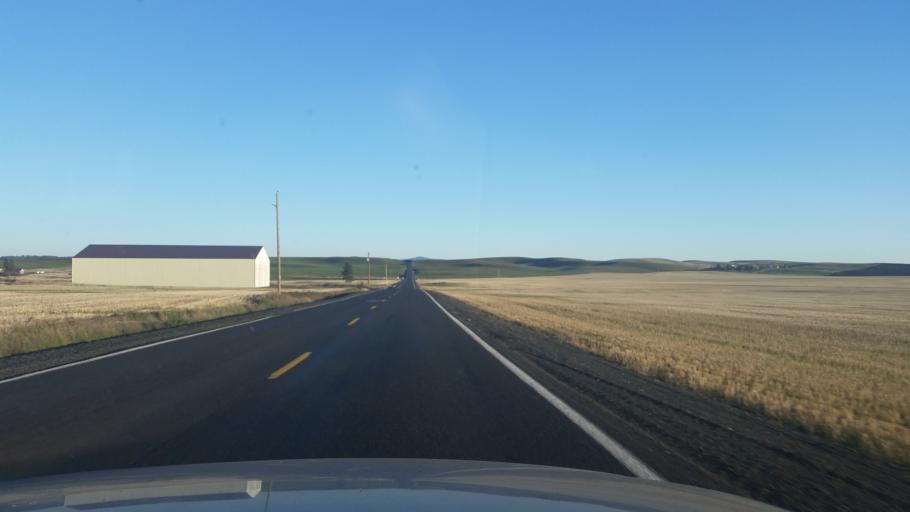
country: US
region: Washington
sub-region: Spokane County
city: Opportunity
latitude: 47.3661
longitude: -117.2895
